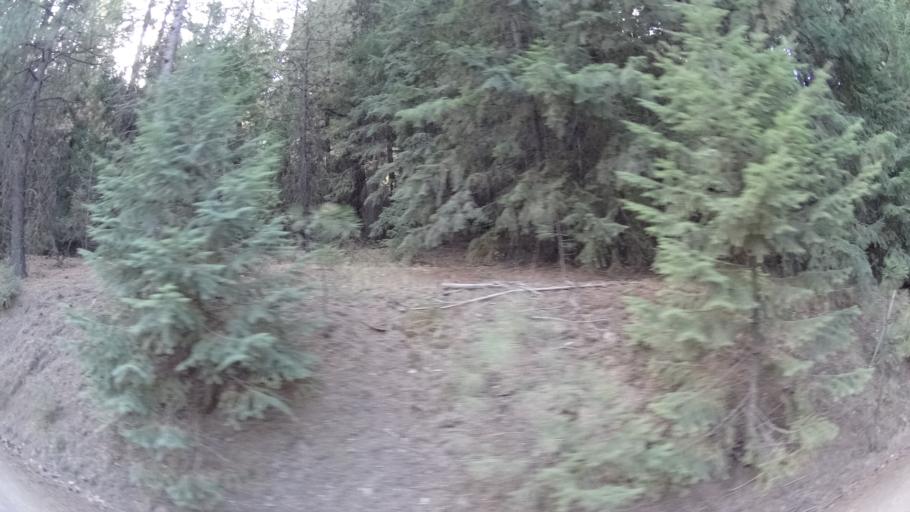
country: US
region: California
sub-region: Siskiyou County
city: Yreka
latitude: 41.7144
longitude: -122.7859
